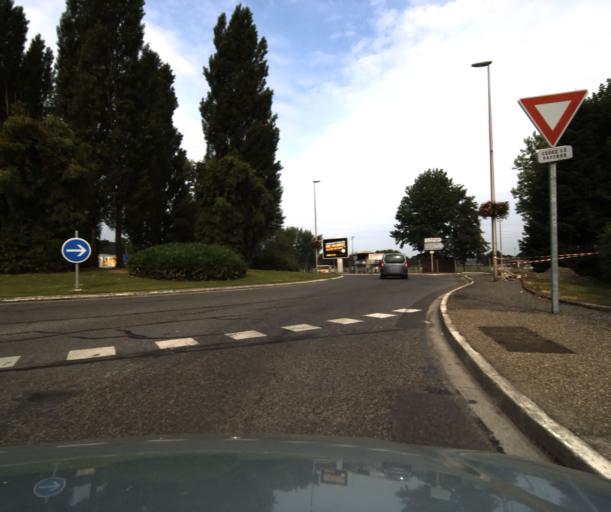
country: FR
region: Midi-Pyrenees
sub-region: Departement des Hautes-Pyrenees
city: Juillan
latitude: 43.2225
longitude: 0.0430
